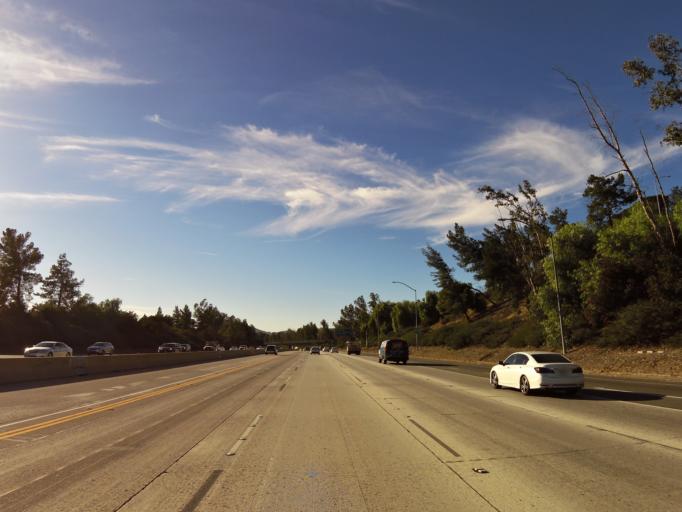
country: US
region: California
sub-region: Los Angeles County
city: Northridge
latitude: 34.2745
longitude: -118.5415
